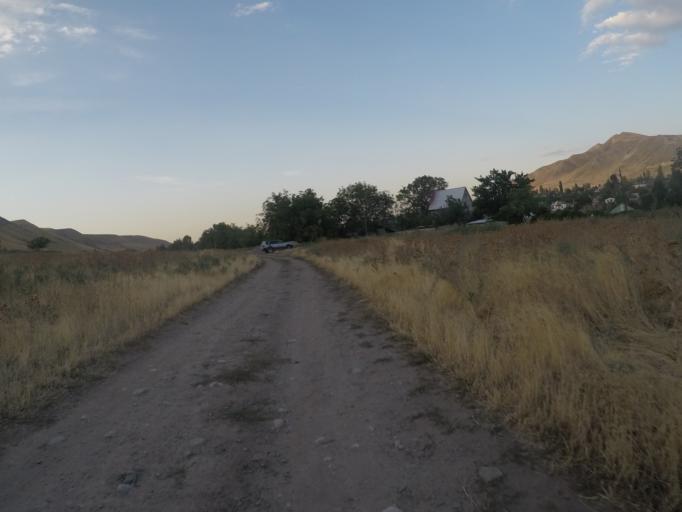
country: KG
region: Chuy
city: Bishkek
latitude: 42.7663
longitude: 74.6383
